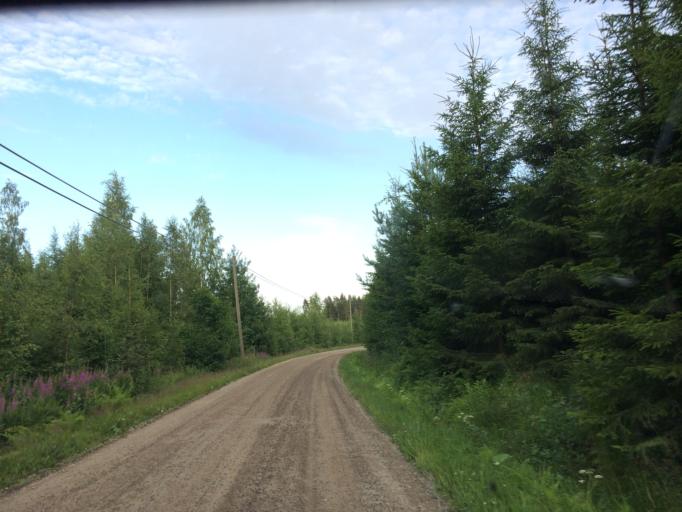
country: FI
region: Haeme
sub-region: Haemeenlinna
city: Janakkala
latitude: 60.8874
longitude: 24.6086
